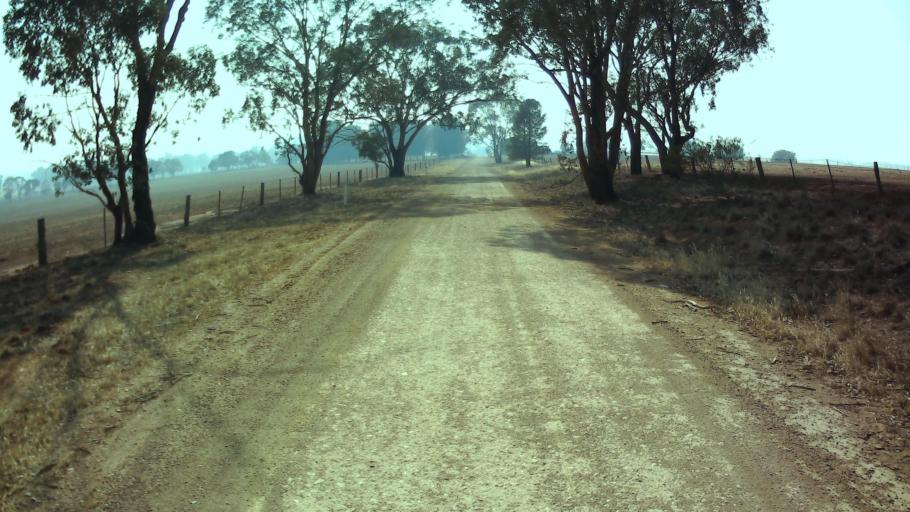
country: AU
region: New South Wales
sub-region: Weddin
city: Grenfell
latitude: -33.9109
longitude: 148.1842
